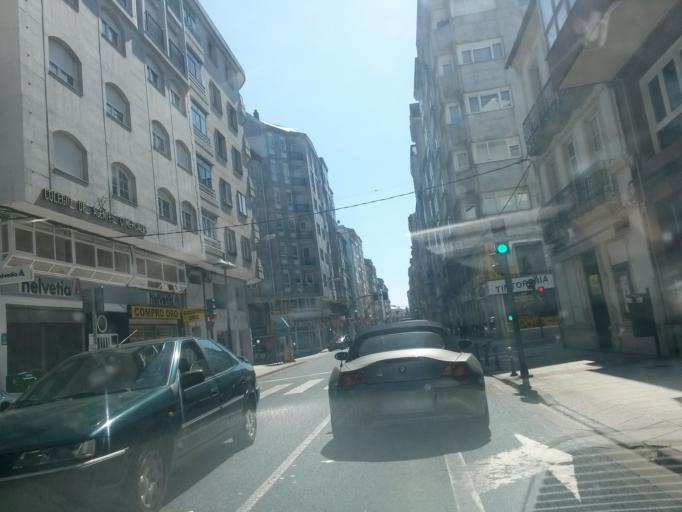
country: ES
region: Galicia
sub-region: Provincia de Lugo
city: Lugo
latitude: 43.0179
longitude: -7.5611
